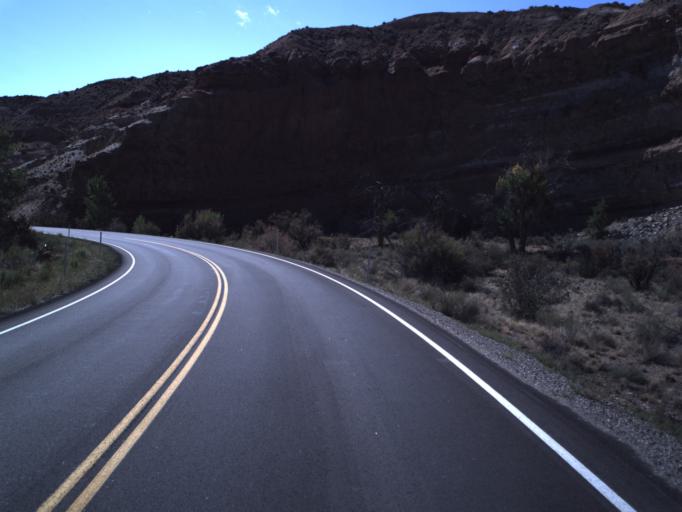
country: US
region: Utah
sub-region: Wayne County
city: Loa
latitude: 38.2859
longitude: -111.1538
